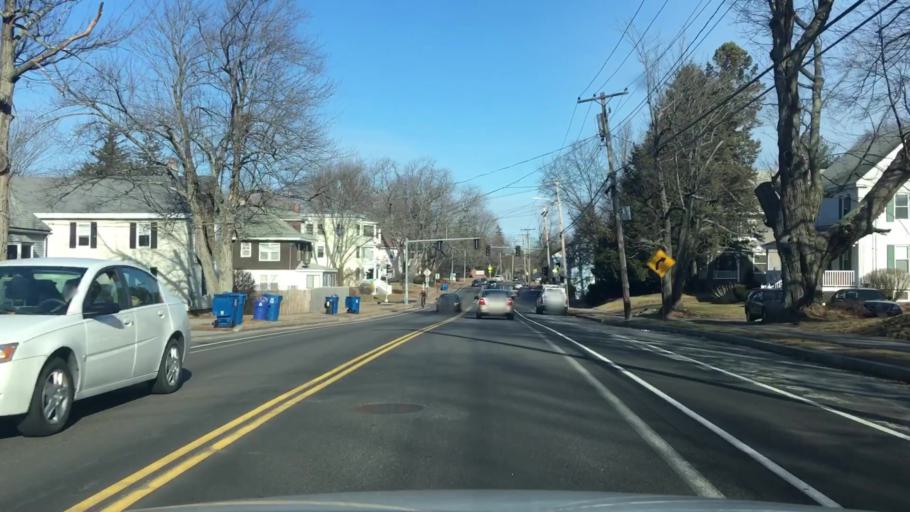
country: US
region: Maine
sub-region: Cumberland County
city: Portland
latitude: 43.6929
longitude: -70.2925
